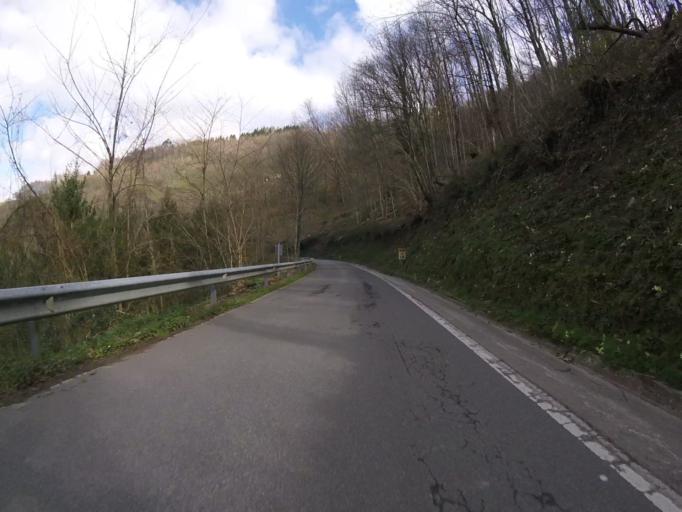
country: ES
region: Navarre
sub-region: Provincia de Navarra
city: Goizueta
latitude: 43.1669
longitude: -1.8581
